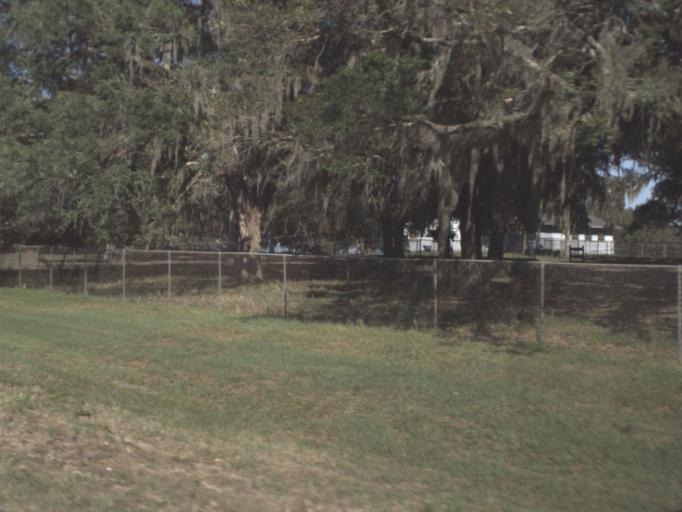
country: US
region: Florida
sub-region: Marion County
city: Dunnellon
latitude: 29.1635
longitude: -82.3423
